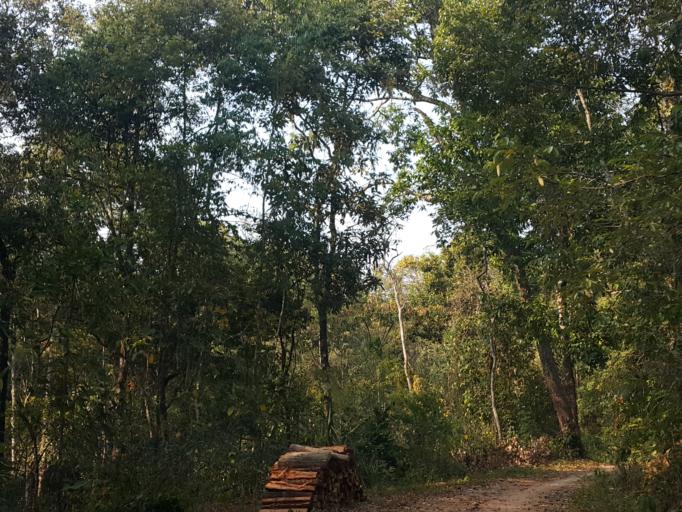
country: TH
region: Chiang Mai
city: Samoeng
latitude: 19.0217
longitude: 98.7615
